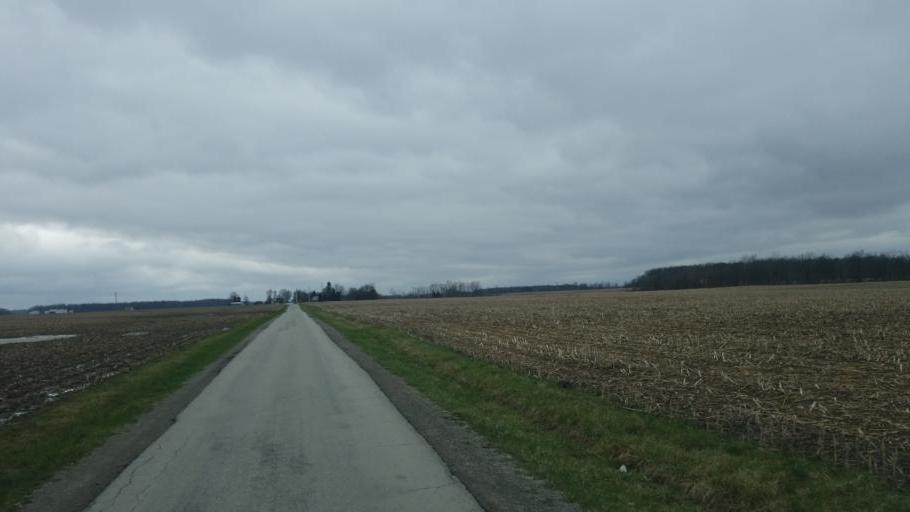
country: US
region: Ohio
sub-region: Hardin County
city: Forest
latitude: 40.7235
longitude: -83.4908
